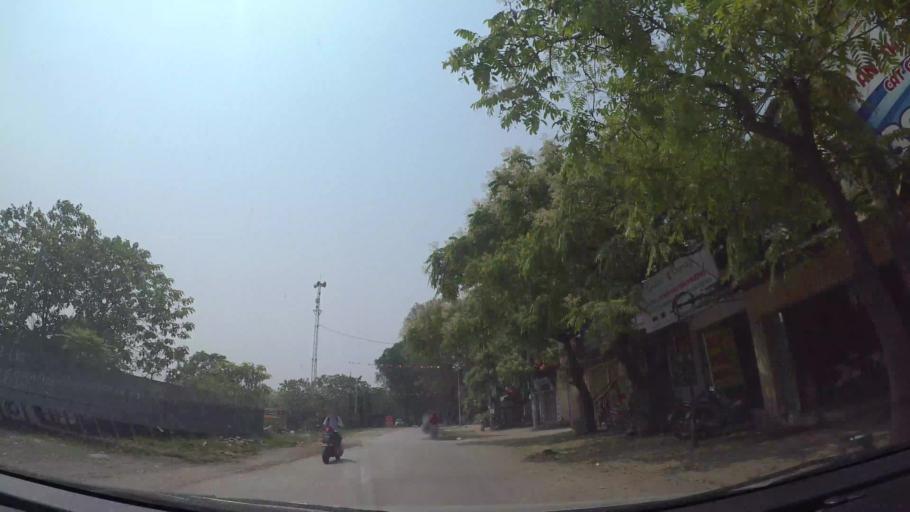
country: VN
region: Ha Noi
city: Ha Dong
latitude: 20.9914
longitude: 105.7630
